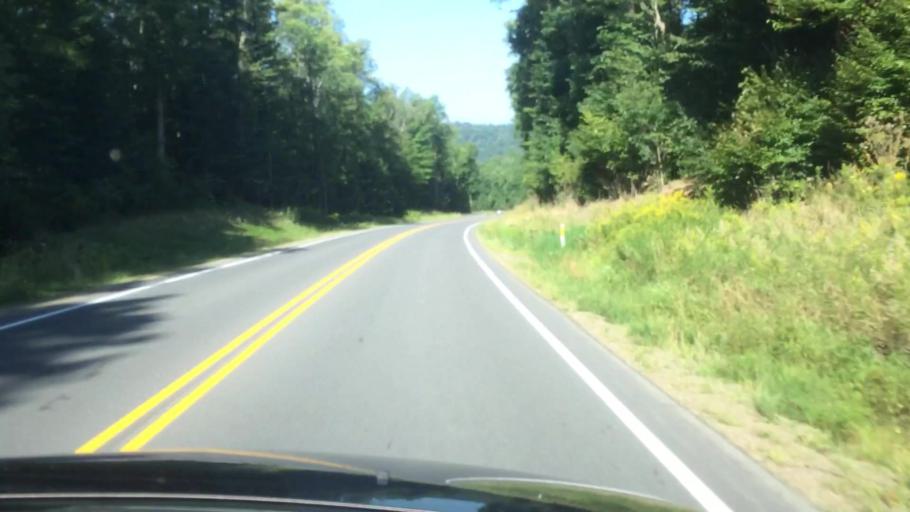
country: US
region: Pennsylvania
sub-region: McKean County
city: Bradford
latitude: 41.8851
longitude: -78.5874
